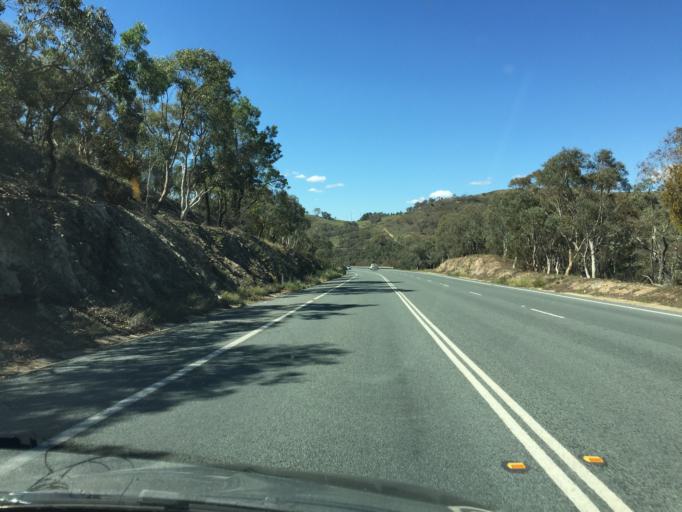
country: AU
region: Australian Capital Territory
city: Macarthur
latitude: -35.4486
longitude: 149.1303
